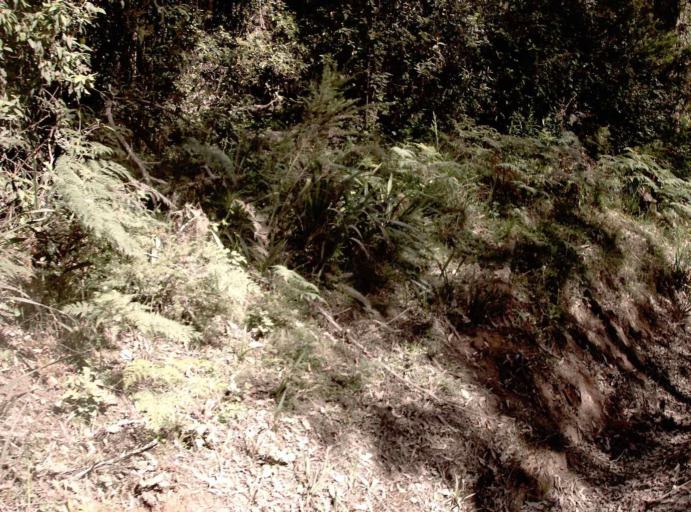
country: AU
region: New South Wales
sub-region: Bombala
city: Bombala
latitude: -37.2421
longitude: 148.7575
